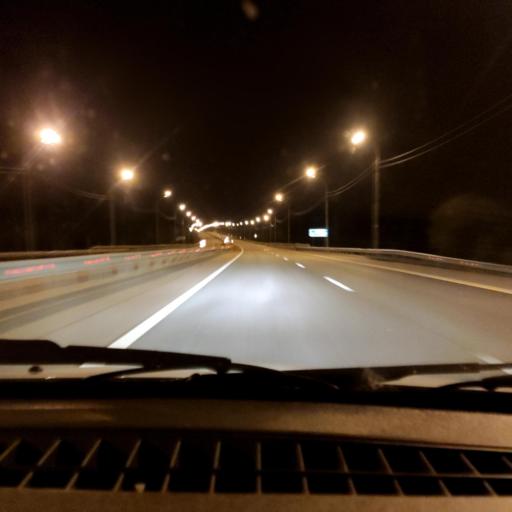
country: RU
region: Lipetsk
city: Zadonsk
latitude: 52.3299
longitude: 39.0147
